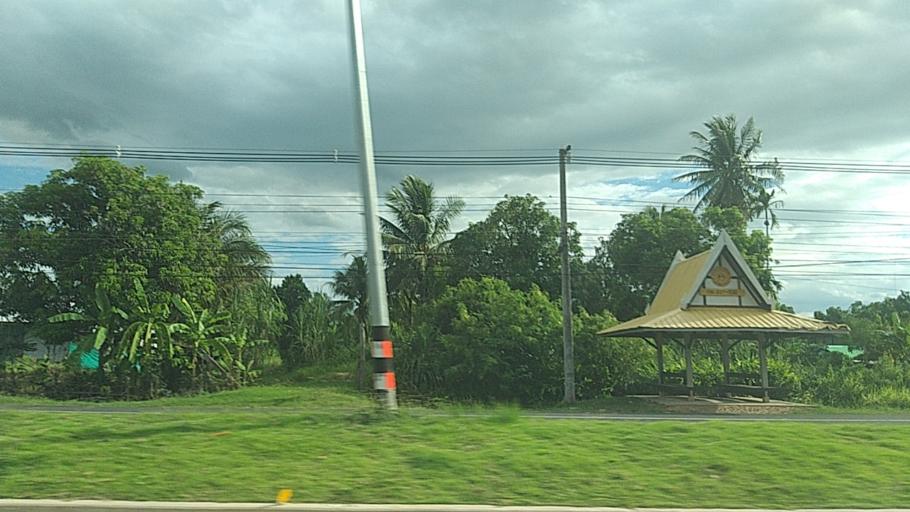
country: TH
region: Surin
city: Prasat
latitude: 14.6059
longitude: 103.4252
